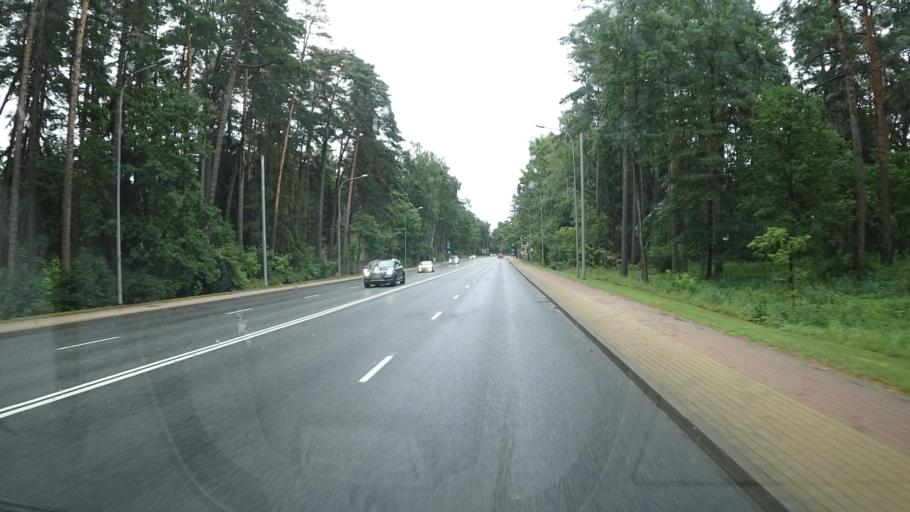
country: LV
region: Babite
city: Pinki
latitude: 56.9746
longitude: 23.8455
